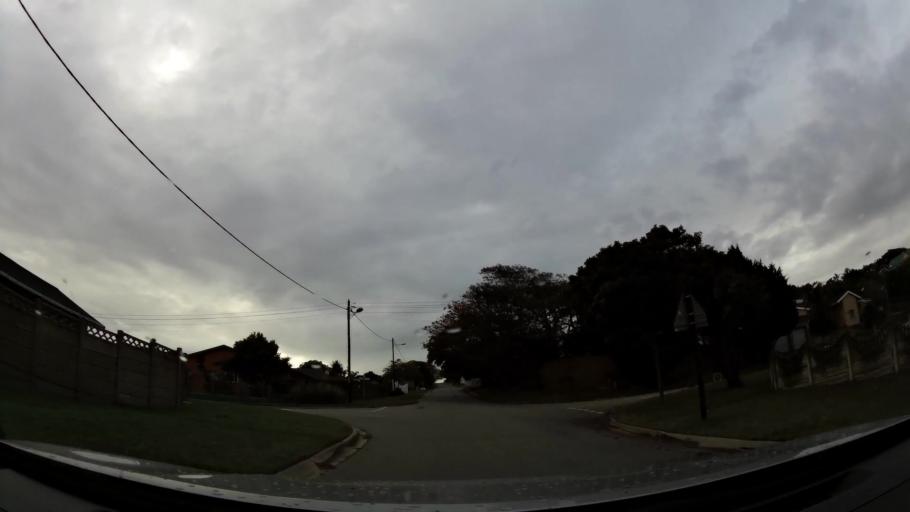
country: ZA
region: Eastern Cape
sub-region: Nelson Mandela Bay Metropolitan Municipality
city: Port Elizabeth
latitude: -34.0010
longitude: 25.5288
